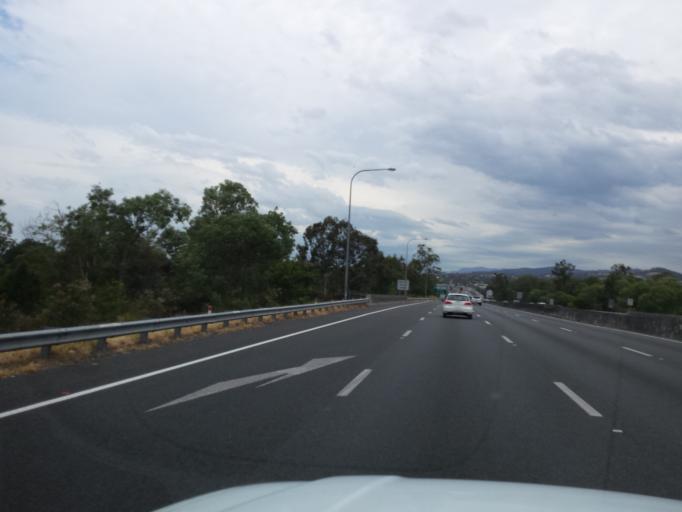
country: AU
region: Queensland
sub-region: Gold Coast
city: Nerang
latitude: -27.9837
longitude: 153.3417
